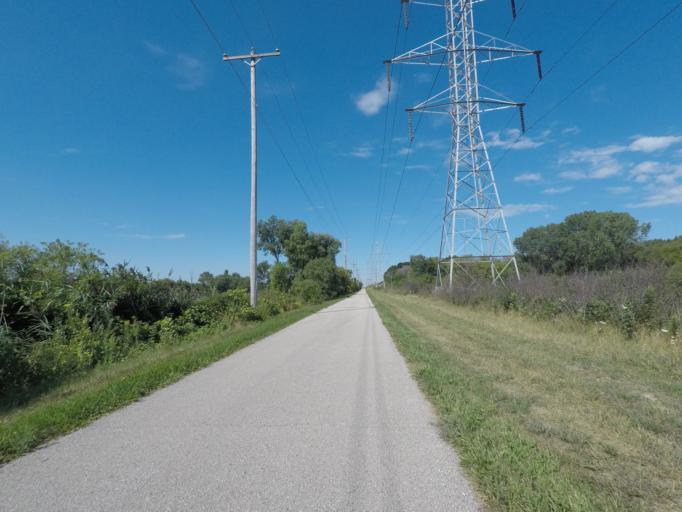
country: US
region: Wisconsin
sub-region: Waukesha County
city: New Berlin
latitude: 43.0100
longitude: -88.1643
